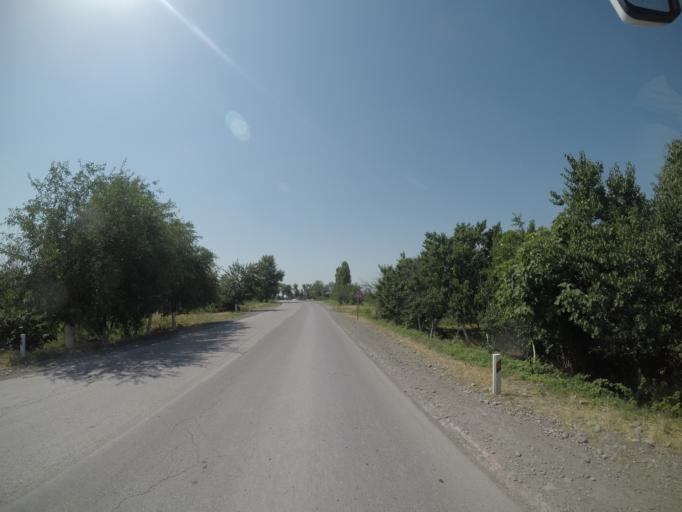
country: AZ
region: Agdas
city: Agdas
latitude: 40.7014
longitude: 47.5415
